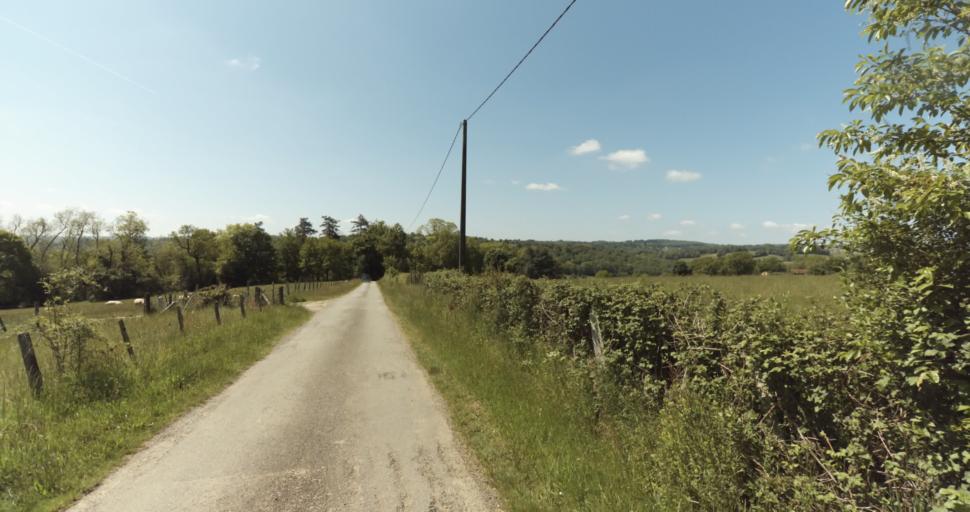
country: FR
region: Limousin
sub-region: Departement de la Haute-Vienne
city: Le Vigen
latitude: 45.7539
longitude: 1.3002
